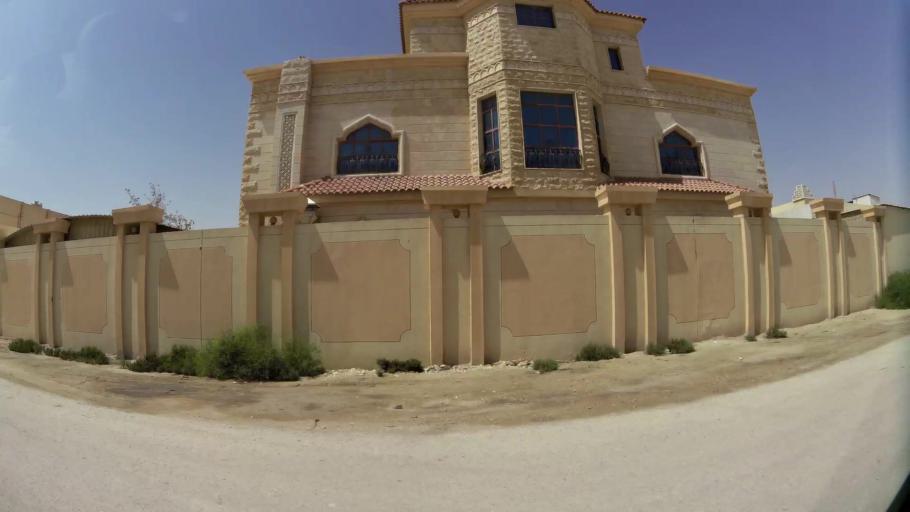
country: QA
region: Baladiyat ar Rayyan
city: Ar Rayyan
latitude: 25.3644
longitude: 51.4784
